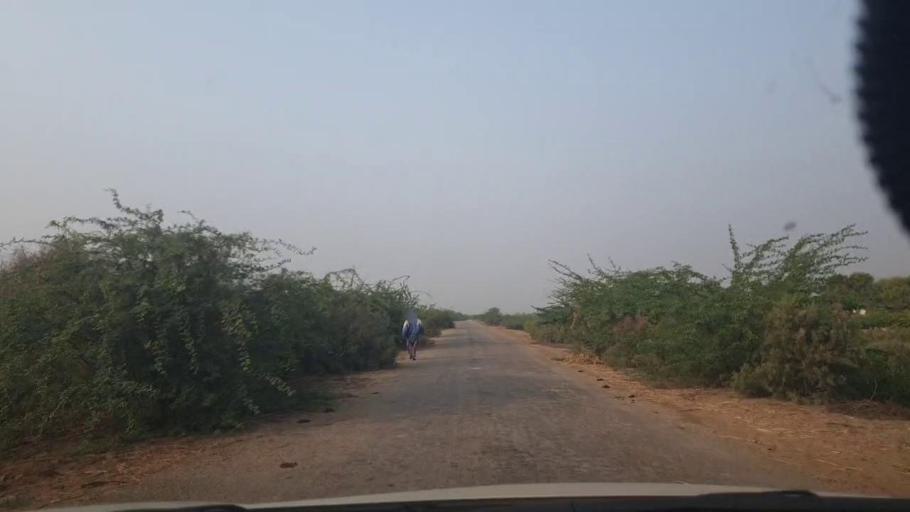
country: PK
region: Sindh
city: Bulri
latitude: 24.8267
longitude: 68.4031
